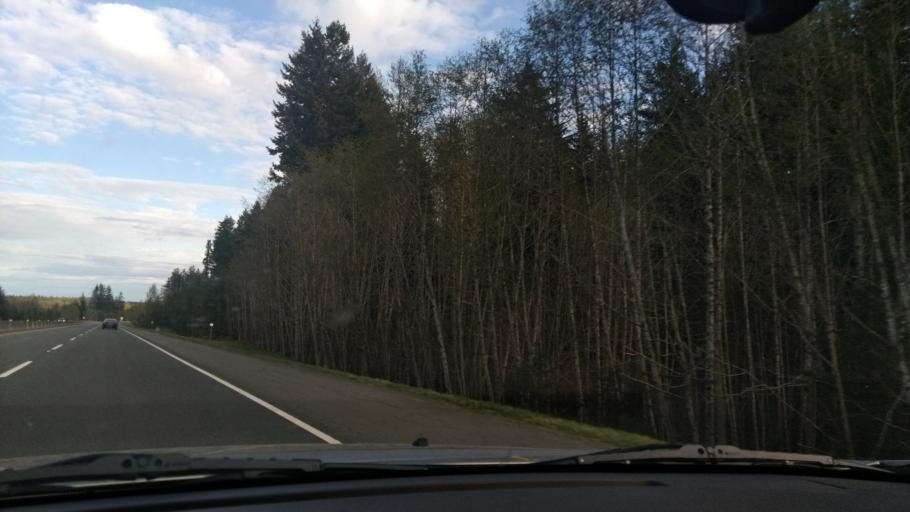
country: CA
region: British Columbia
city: Campbell River
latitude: 49.8223
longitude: -125.1855
